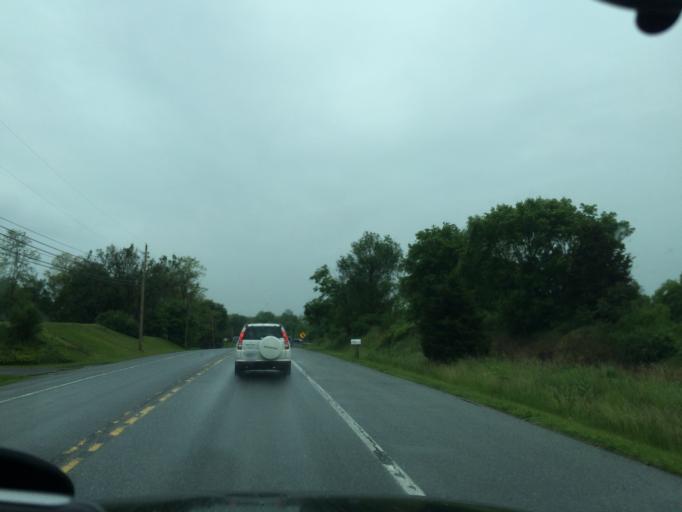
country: US
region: Maryland
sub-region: Washington County
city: Robinwood
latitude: 39.6421
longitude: -77.6445
